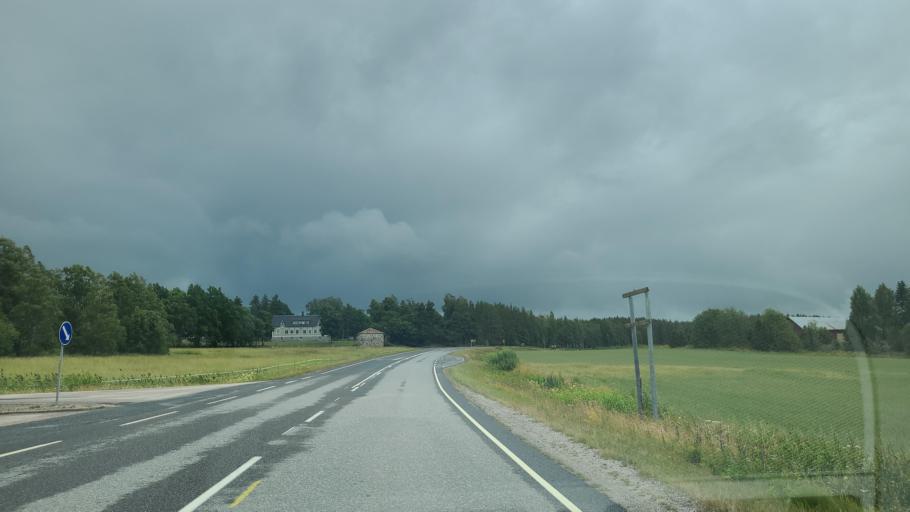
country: FI
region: Varsinais-Suomi
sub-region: Turku
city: Sauvo
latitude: 60.3308
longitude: 22.7125
